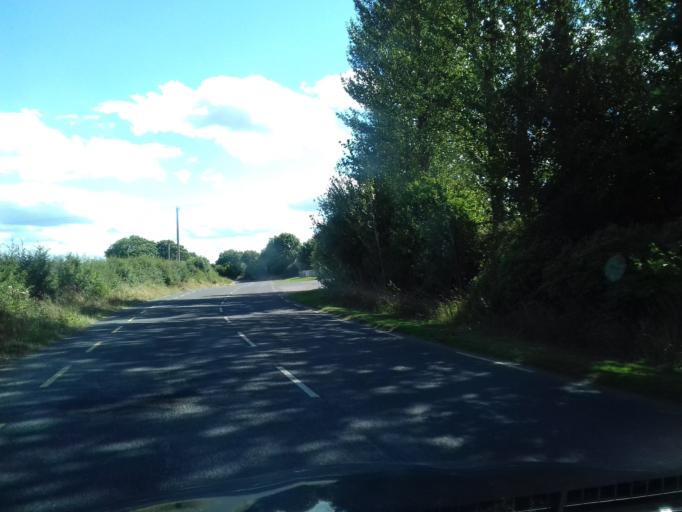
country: IE
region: Leinster
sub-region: Kilkenny
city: Callan
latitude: 52.5394
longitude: -7.3809
